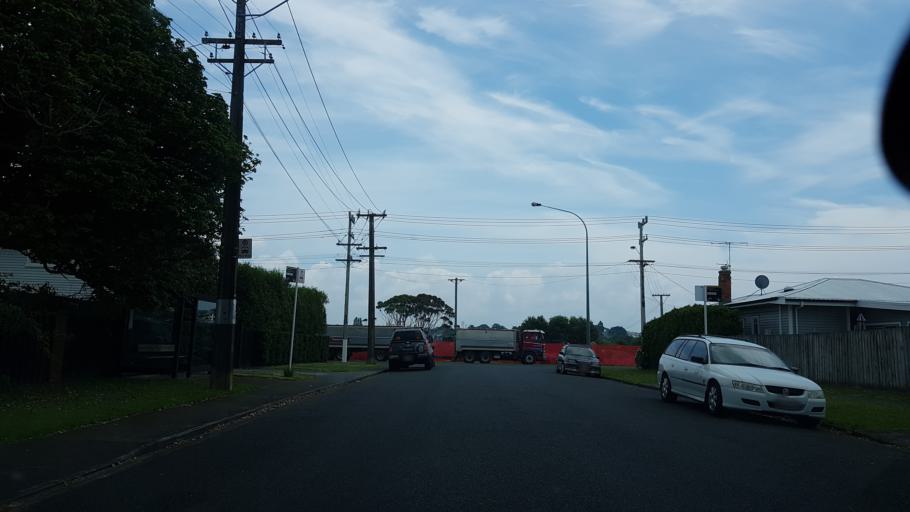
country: NZ
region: Auckland
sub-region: Auckland
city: North Shore
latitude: -36.8055
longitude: 174.7832
